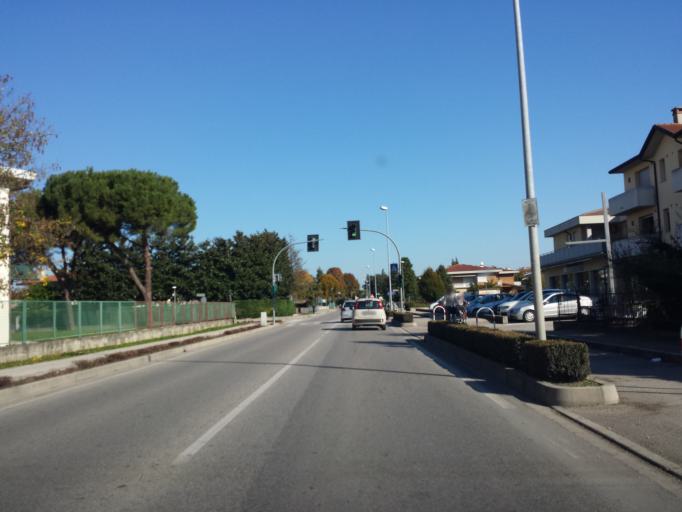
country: IT
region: Veneto
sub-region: Provincia di Vicenza
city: Camisano Vicentino
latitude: 45.5200
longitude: 11.7165
